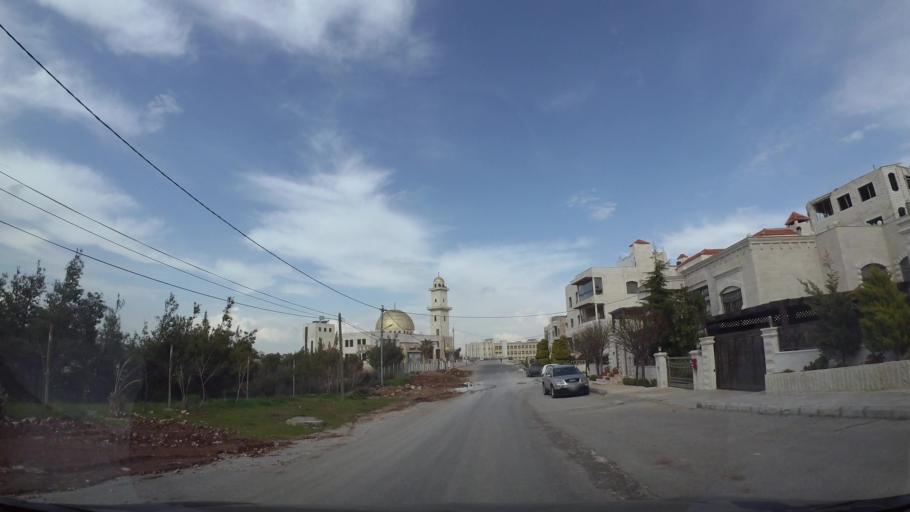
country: JO
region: Amman
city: Amman
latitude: 32.0149
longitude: 35.9392
